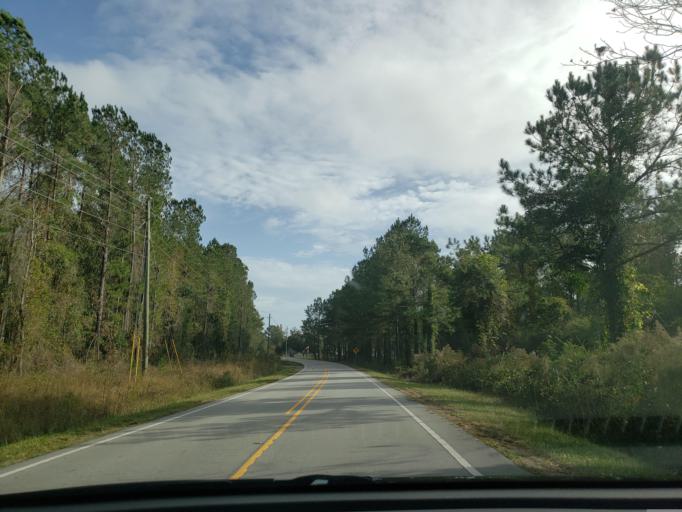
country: US
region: North Carolina
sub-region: Onslow County
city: Jacksonville
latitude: 34.6724
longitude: -77.4996
